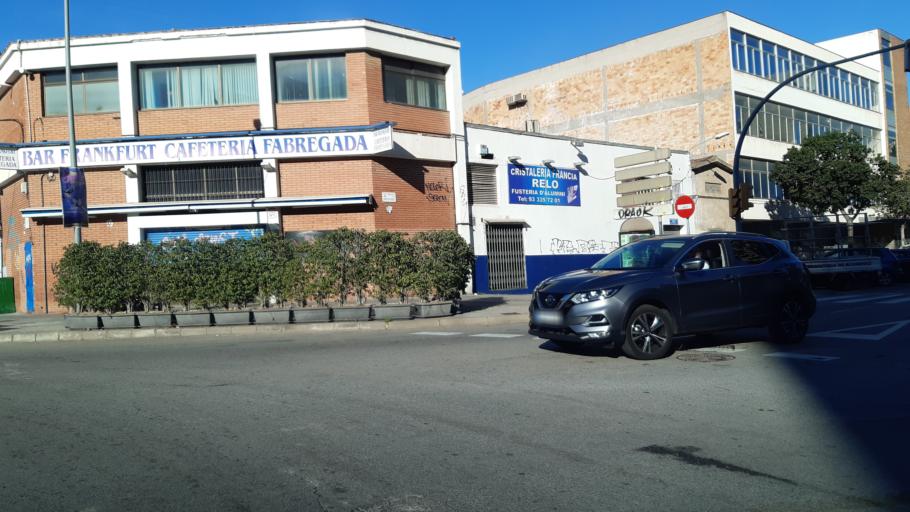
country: ES
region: Catalonia
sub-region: Provincia de Barcelona
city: L'Hospitalet de Llobregat
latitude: 41.3559
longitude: 2.1110
